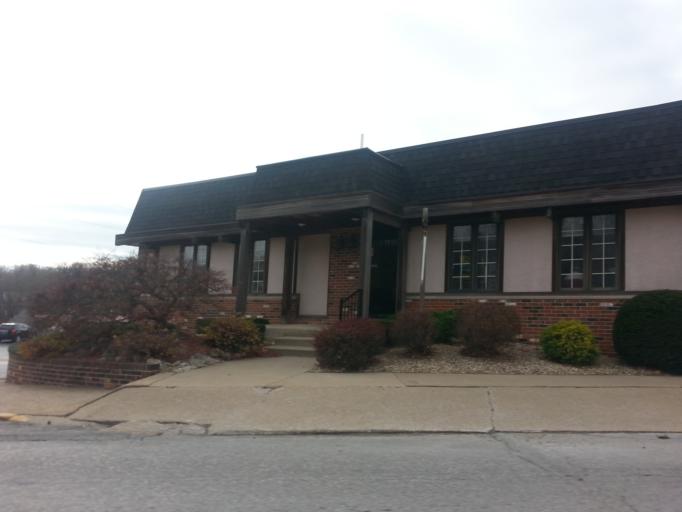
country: US
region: Missouri
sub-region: Marion County
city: Hannibal
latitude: 39.7060
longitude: -91.3863
